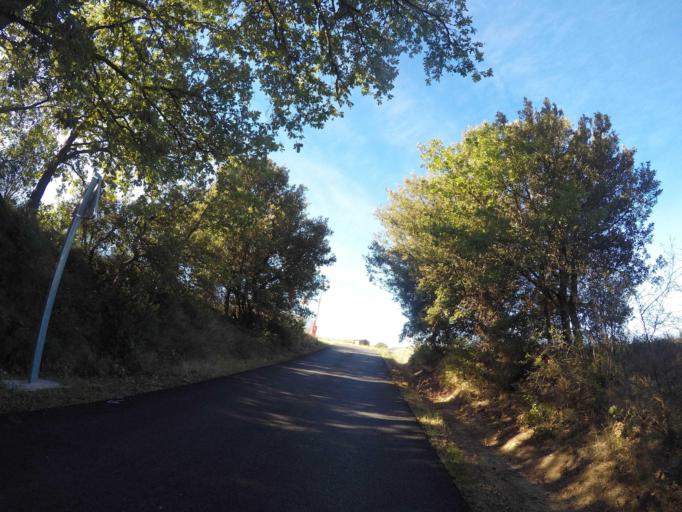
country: FR
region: Languedoc-Roussillon
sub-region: Departement des Pyrenees-Orientales
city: Llupia
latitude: 42.6016
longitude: 2.7674
